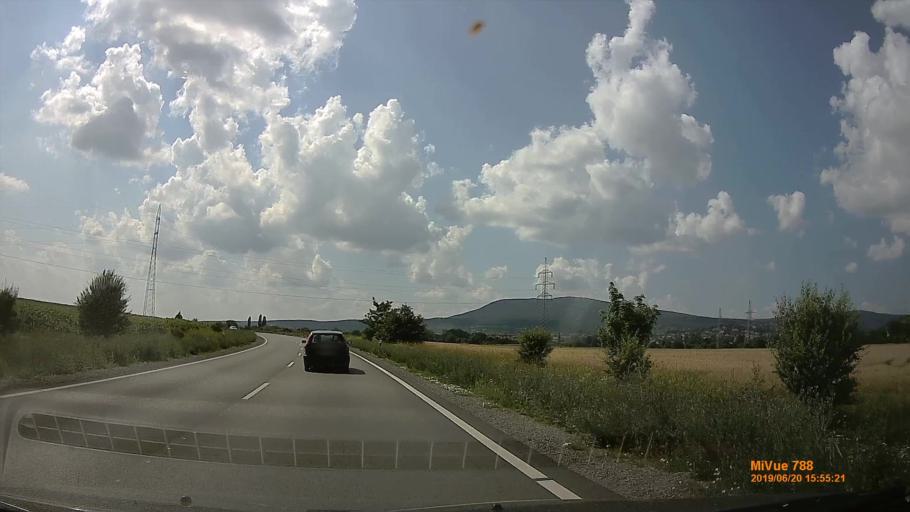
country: HU
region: Baranya
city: Pellerd
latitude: 46.0543
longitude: 18.1931
